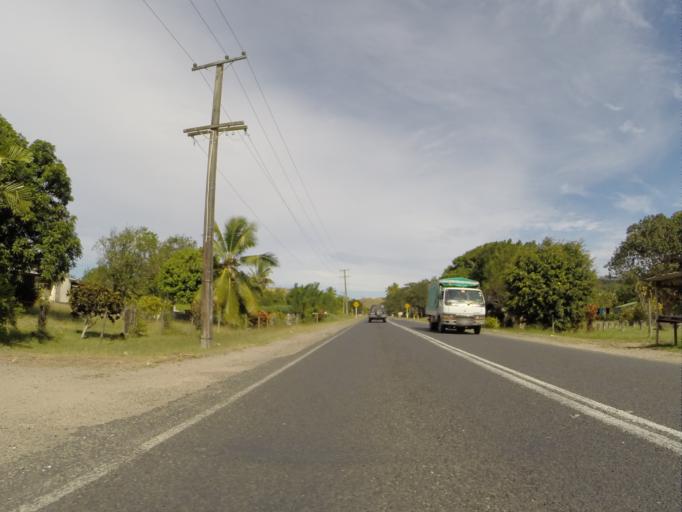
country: FJ
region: Western
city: Nadi
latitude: -18.1574
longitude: 177.4914
